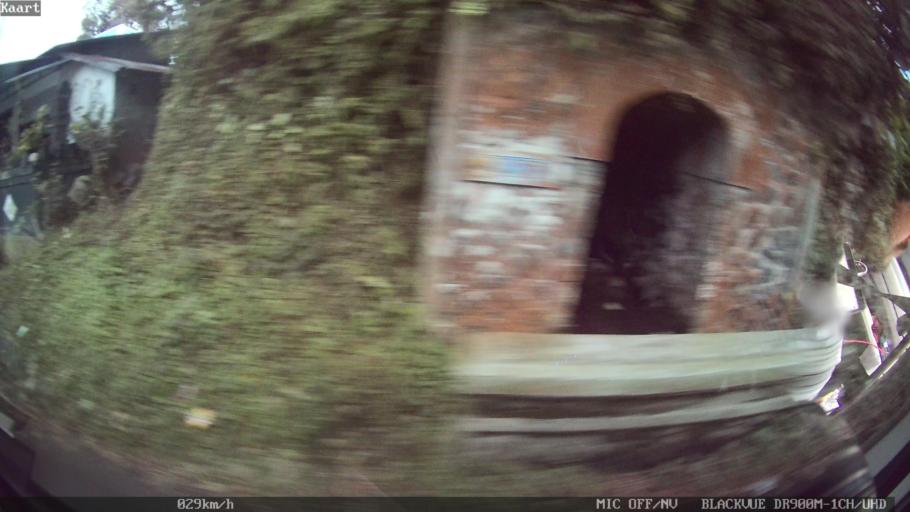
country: ID
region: Bali
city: Peneng
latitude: -8.3519
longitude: 115.2060
